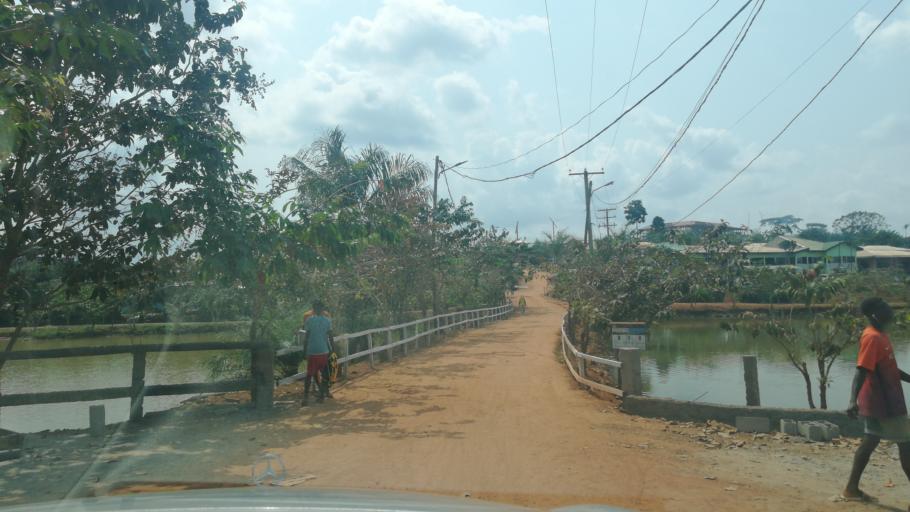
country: CM
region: Centre
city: Yaounde
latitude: 3.7860
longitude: 11.4884
